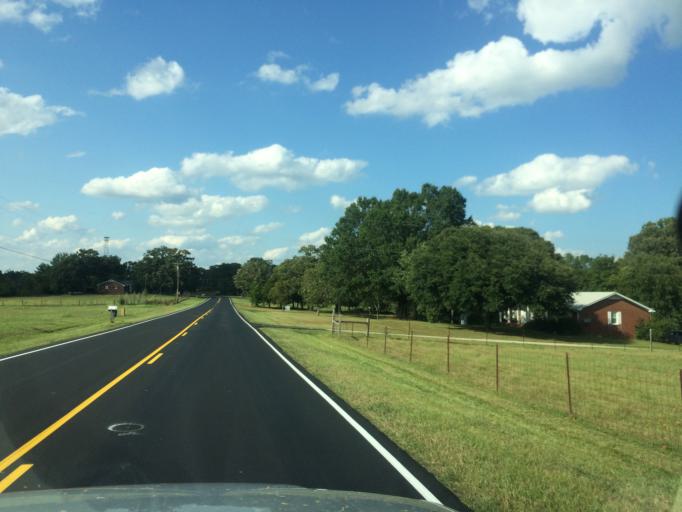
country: US
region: South Carolina
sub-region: Greenwood County
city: Ware Shoals
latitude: 34.4970
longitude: -82.1793
